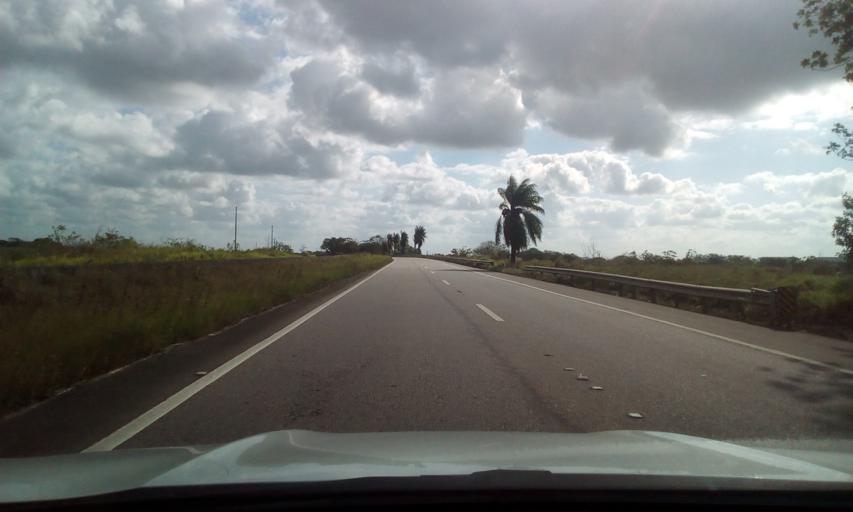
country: BR
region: Pernambuco
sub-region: Itapissuma
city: Itapissuma
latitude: -7.7184
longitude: -34.9393
